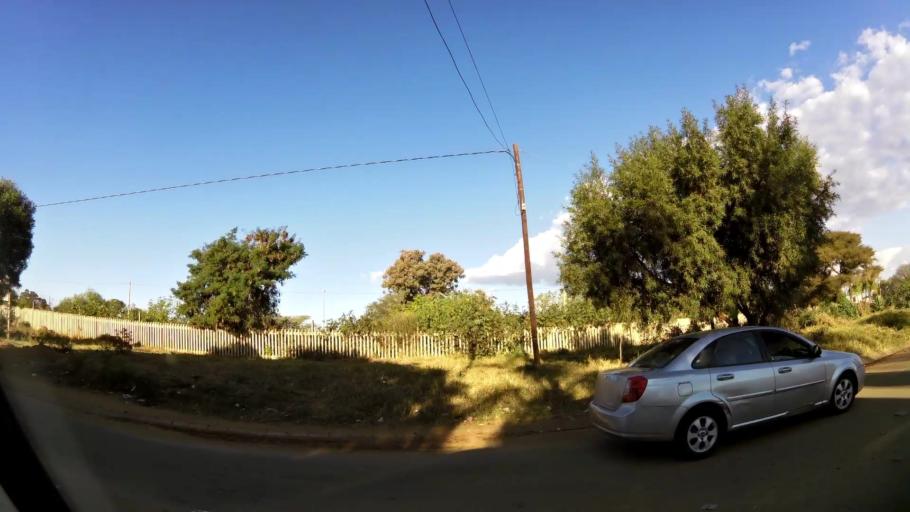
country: ZA
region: Limpopo
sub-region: Waterberg District Municipality
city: Mokopane
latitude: -24.1551
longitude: 28.9853
